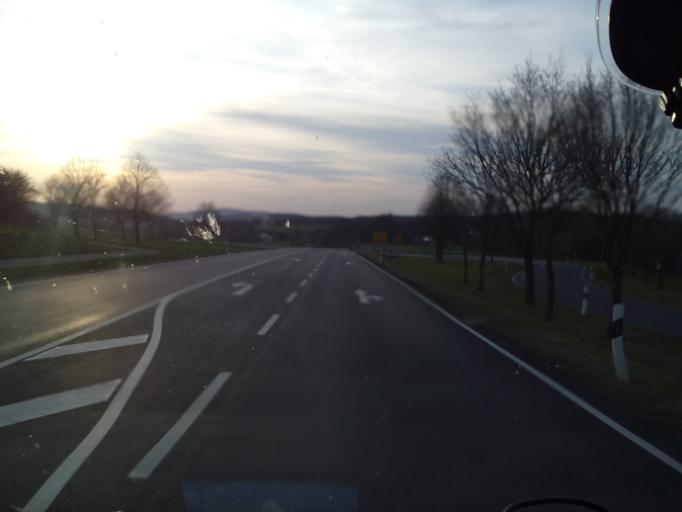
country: DE
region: Bavaria
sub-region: Regierungsbezirk Unterfranken
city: Pfarrweisach
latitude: 50.1395
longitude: 10.7491
